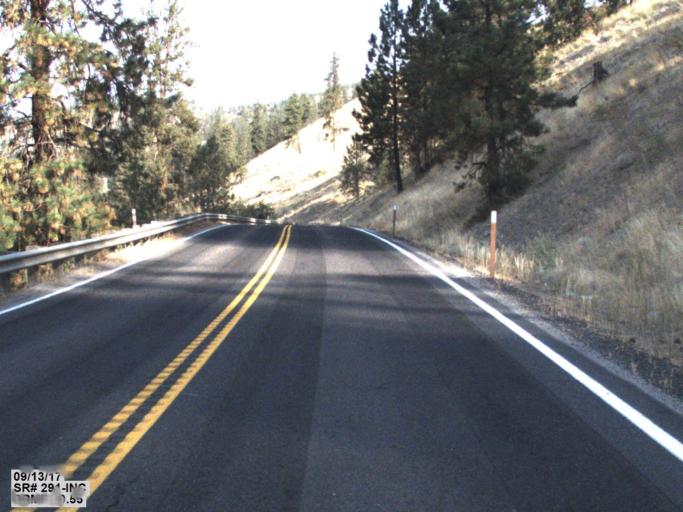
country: US
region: Washington
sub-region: Spokane County
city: Fairwood
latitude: 47.7895
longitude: -117.5279
